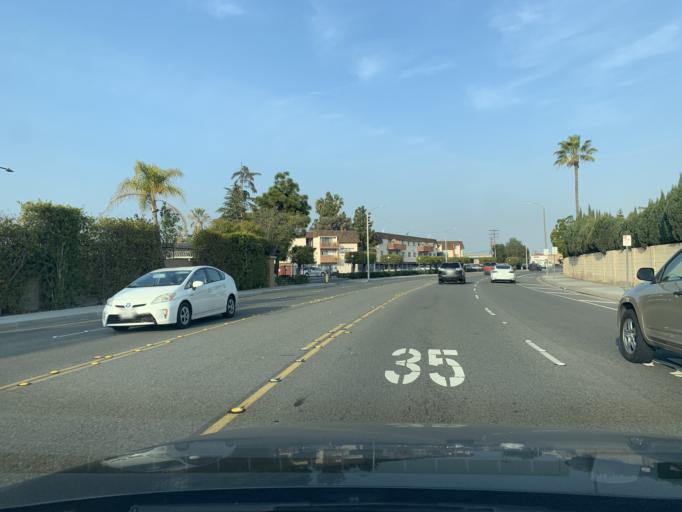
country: US
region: California
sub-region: Orange County
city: Westminster
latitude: 33.7710
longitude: -118.0253
